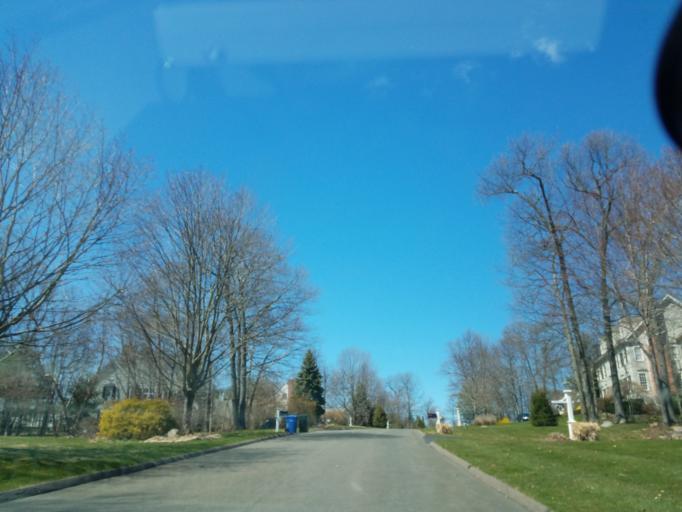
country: US
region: Connecticut
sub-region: Hartford County
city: Collinsville
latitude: 41.7879
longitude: -72.9014
